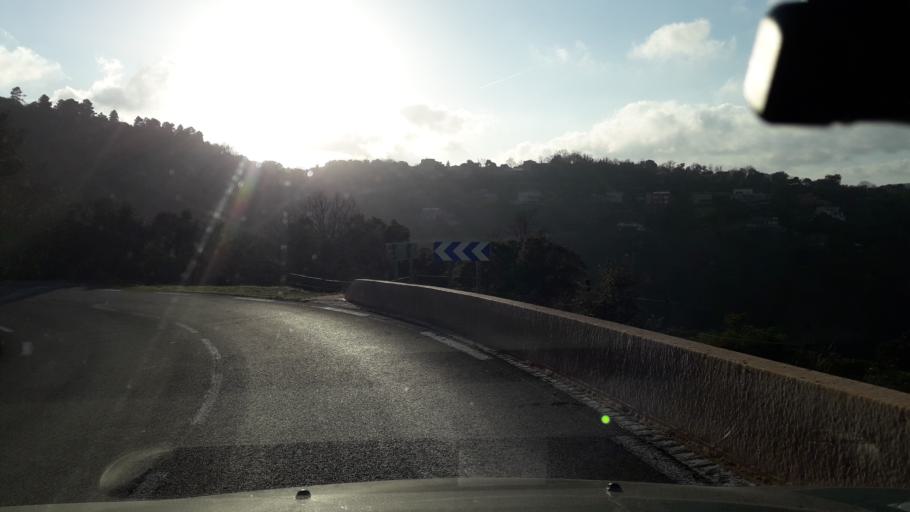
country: FR
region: Provence-Alpes-Cote d'Azur
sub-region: Departement du Var
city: Tanneron
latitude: 43.5157
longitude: 6.8182
